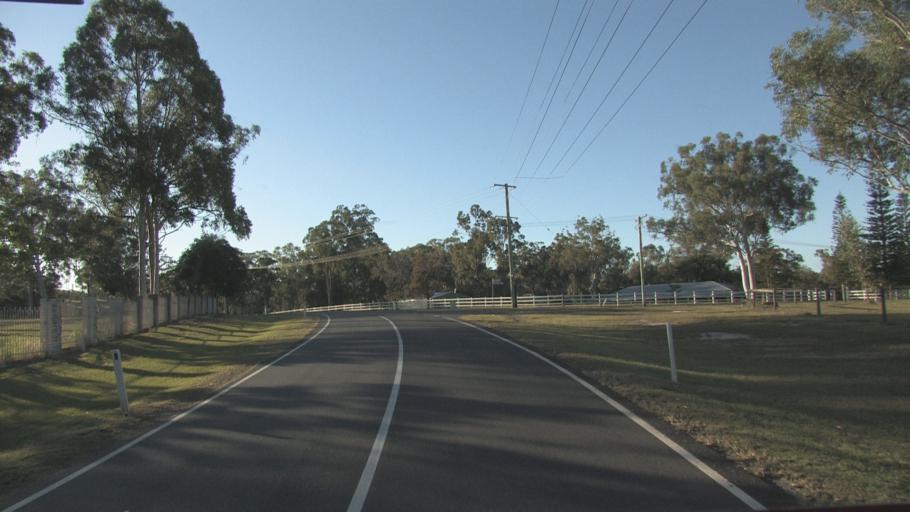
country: AU
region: Queensland
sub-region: Redland
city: Redland Bay
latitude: -27.6613
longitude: 153.2771
